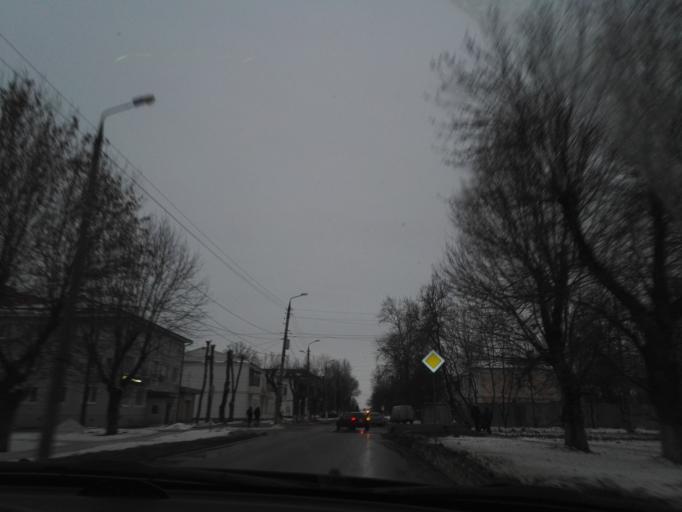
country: RU
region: Tula
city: Novomoskovsk
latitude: 54.0089
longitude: 38.3004
